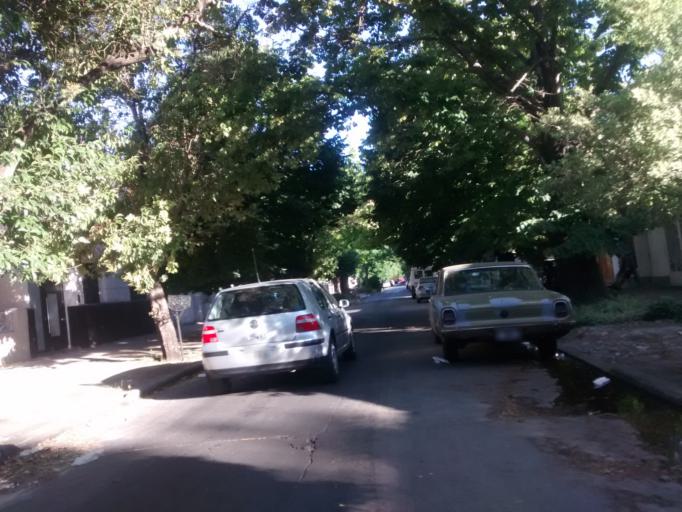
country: AR
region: Buenos Aires
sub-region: Partido de La Plata
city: La Plata
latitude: -34.9337
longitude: -57.9450
